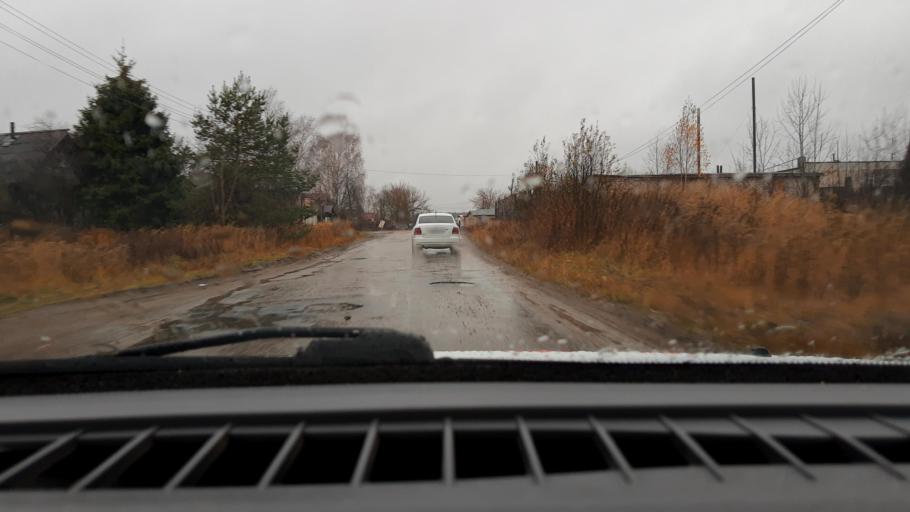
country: RU
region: Nizjnij Novgorod
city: Linda
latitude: 56.6832
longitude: 44.1991
